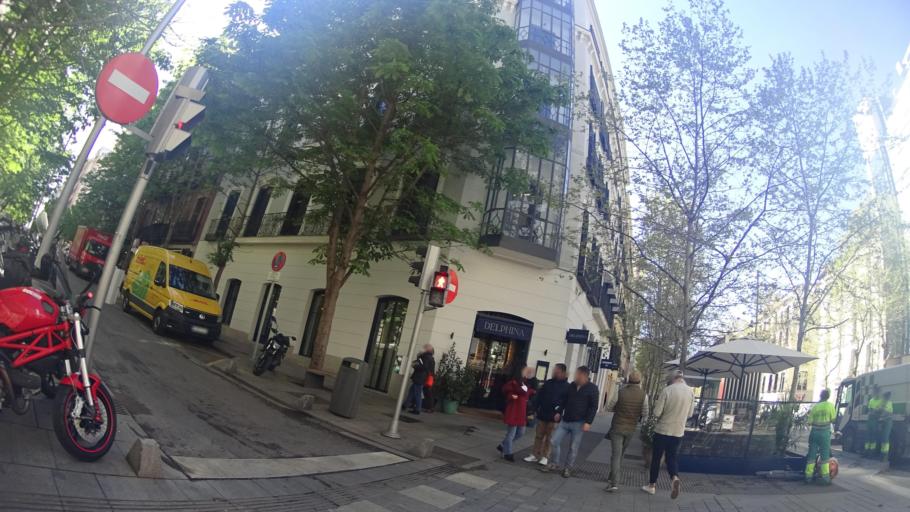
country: ES
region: Madrid
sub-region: Provincia de Madrid
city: Salamanca
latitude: 40.4318
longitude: -3.6865
